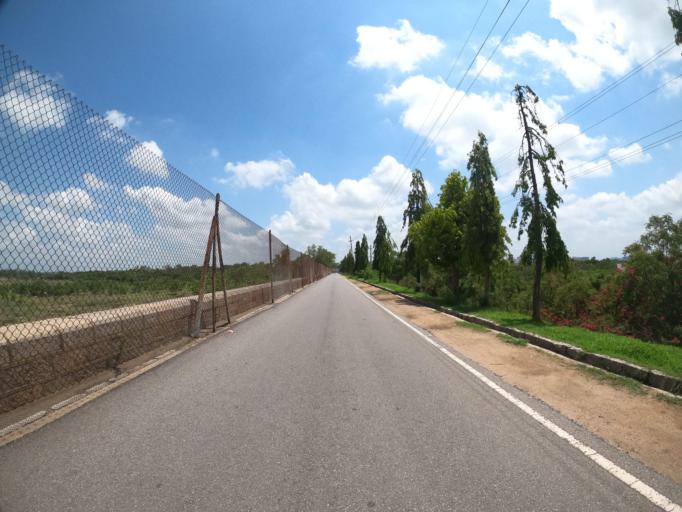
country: IN
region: Telangana
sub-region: Medak
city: Serilingampalle
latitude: 17.3839
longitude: 78.3167
